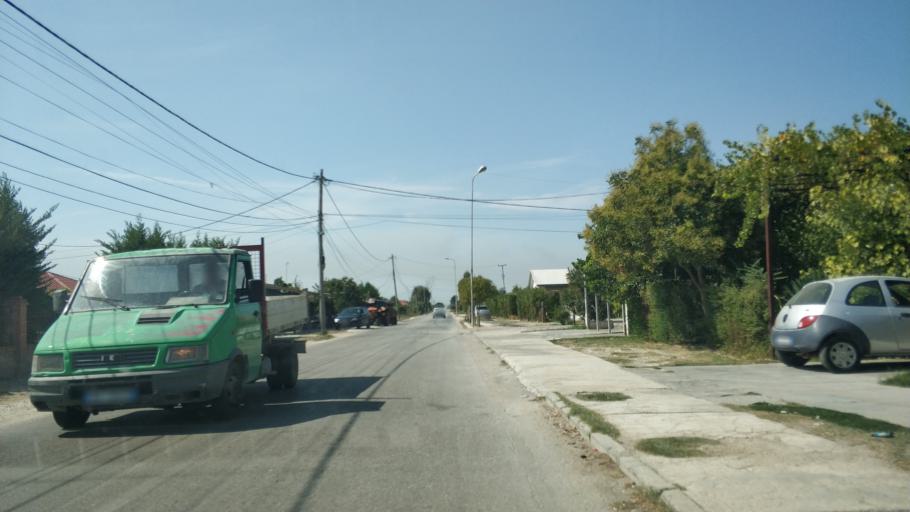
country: AL
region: Fier
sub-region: Rrethi i Fierit
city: Dermenas
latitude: 40.7459
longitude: 19.4917
